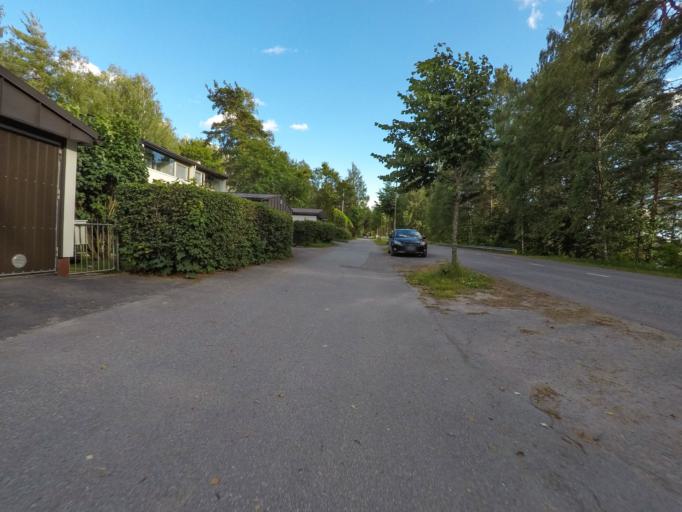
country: FI
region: South Karelia
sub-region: Lappeenranta
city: Lappeenranta
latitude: 61.0679
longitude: 28.1568
